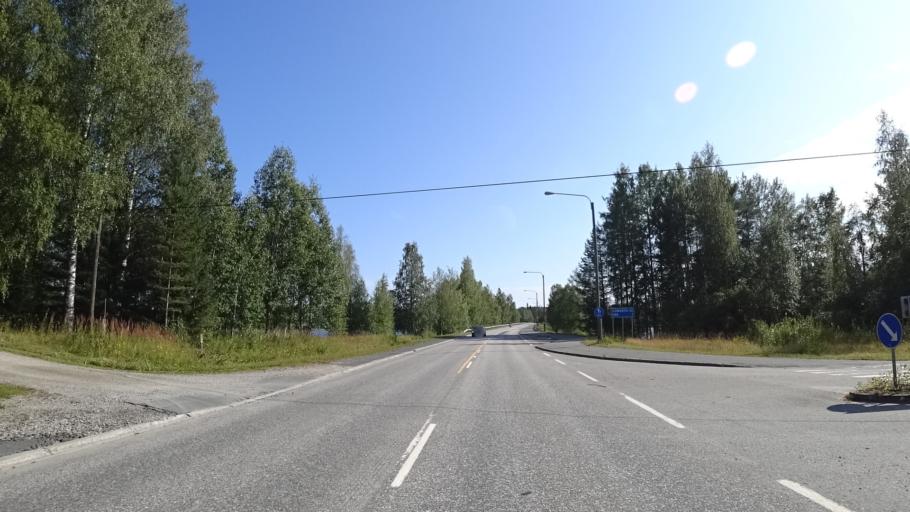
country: FI
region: North Karelia
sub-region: Joensuu
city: Eno
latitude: 62.8073
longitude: 30.1515
